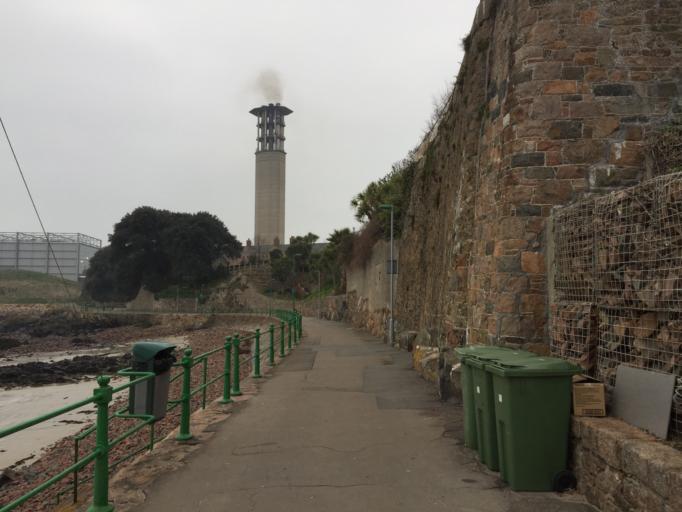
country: JE
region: St Helier
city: Saint Helier
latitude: 49.1763
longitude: -2.1059
